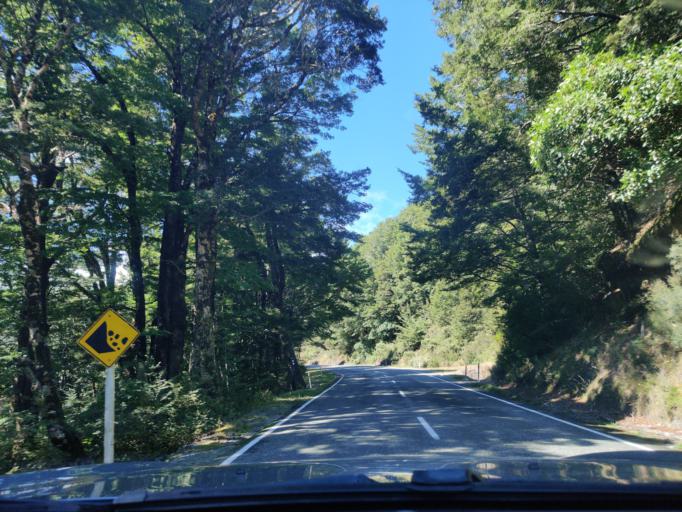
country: NZ
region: Canterbury
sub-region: Hurunui District
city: Amberley
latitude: -42.3744
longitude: 172.3694
